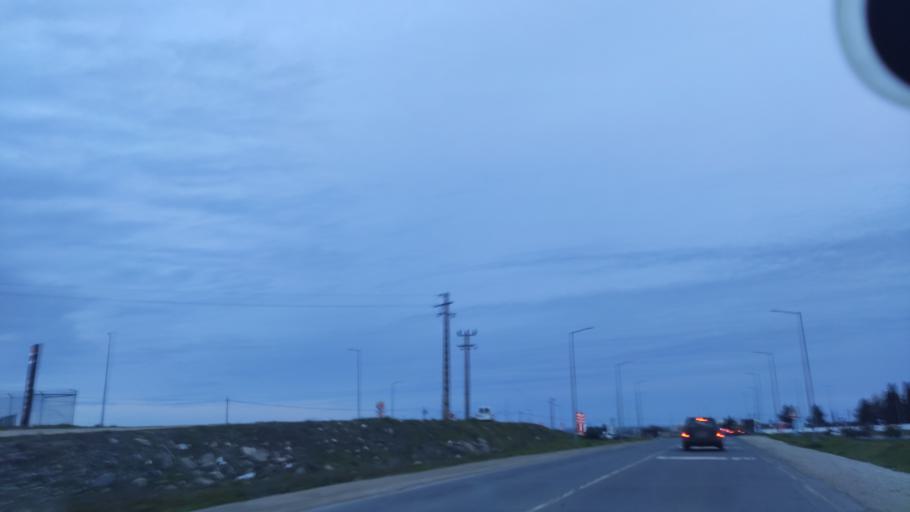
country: PT
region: Beja
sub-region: Beja
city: Beja
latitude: 38.0210
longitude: -7.8496
